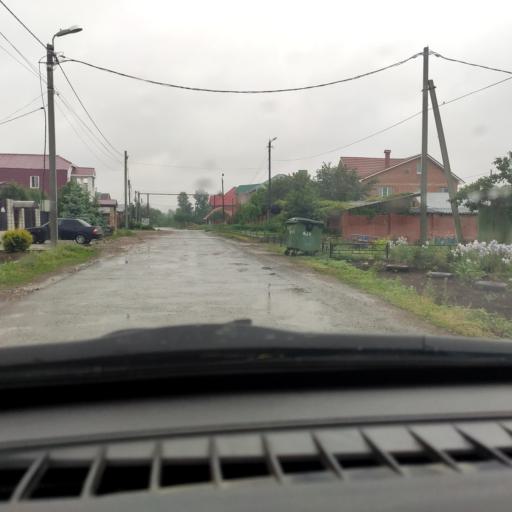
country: RU
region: Samara
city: Tol'yatti
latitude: 53.5626
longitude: 49.3809
